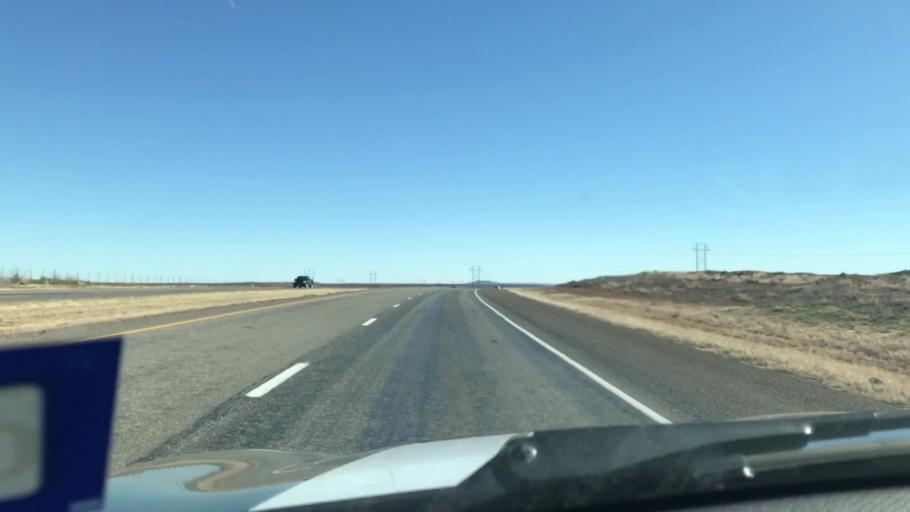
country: US
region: Texas
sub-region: Garza County
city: Post
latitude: 33.1192
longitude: -101.2803
